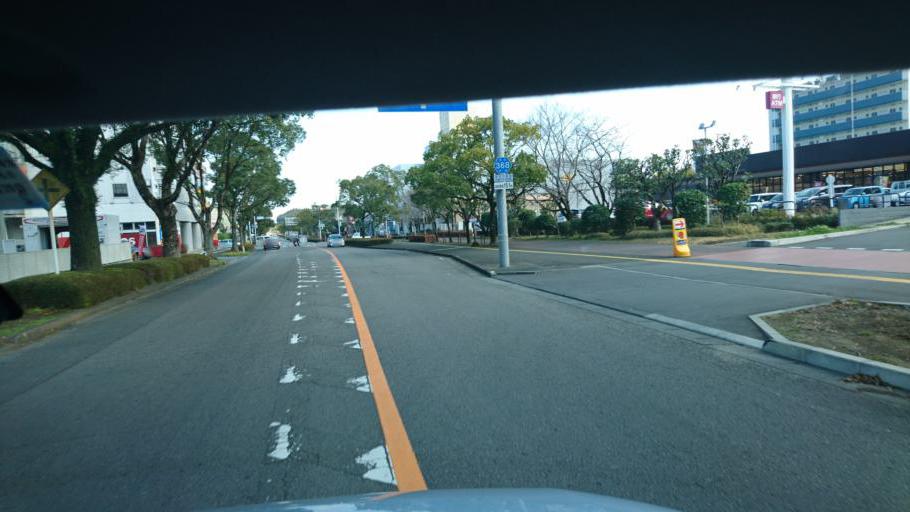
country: JP
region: Miyazaki
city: Miyazaki-shi
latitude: 31.8314
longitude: 131.4189
